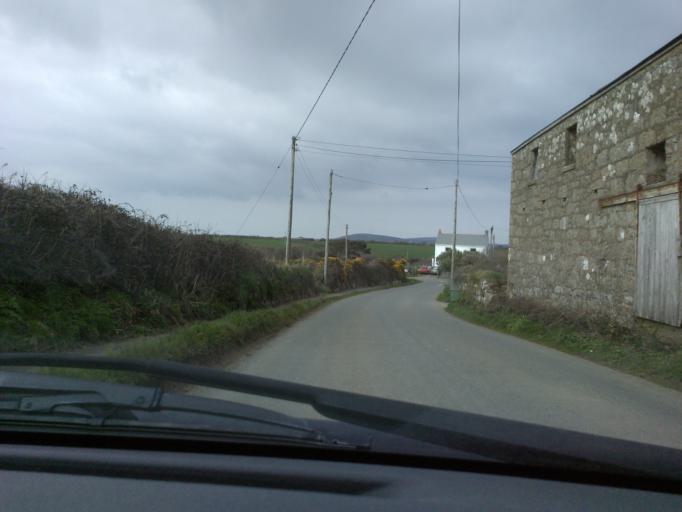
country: GB
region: England
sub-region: Cornwall
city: St. Buryan
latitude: 50.0549
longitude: -5.6585
